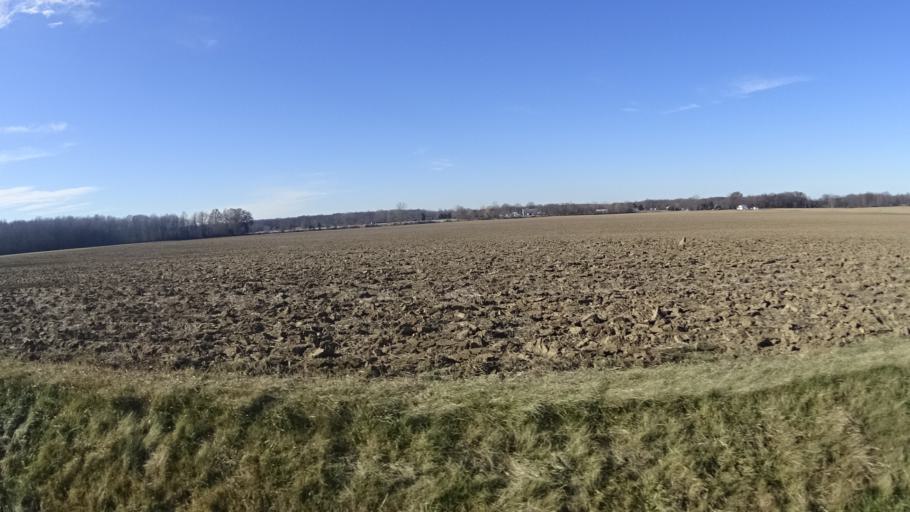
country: US
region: Ohio
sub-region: Lorain County
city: South Amherst
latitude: 41.3110
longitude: -82.2877
